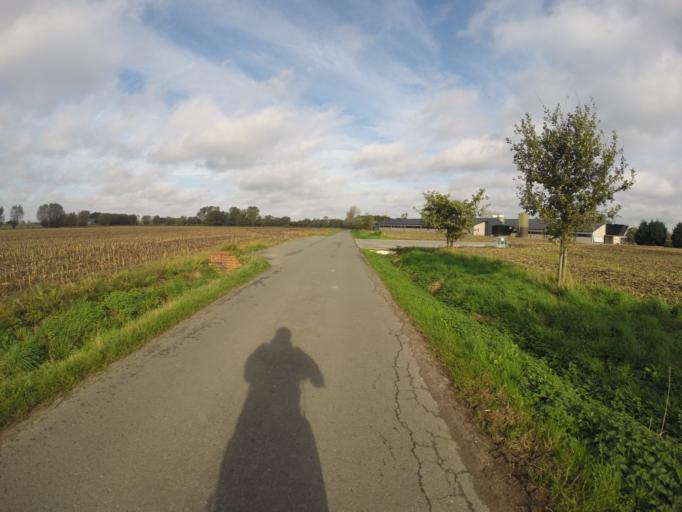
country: BE
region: Flanders
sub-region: Provincie Oost-Vlaanderen
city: Knesselare
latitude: 51.1181
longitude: 3.4172
